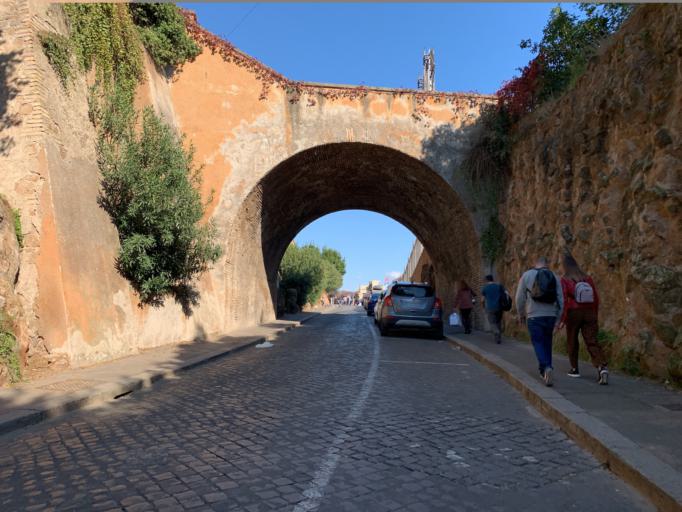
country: IT
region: Latium
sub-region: Citta metropolitana di Roma Capitale
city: Rome
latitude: 41.8919
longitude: 12.4830
